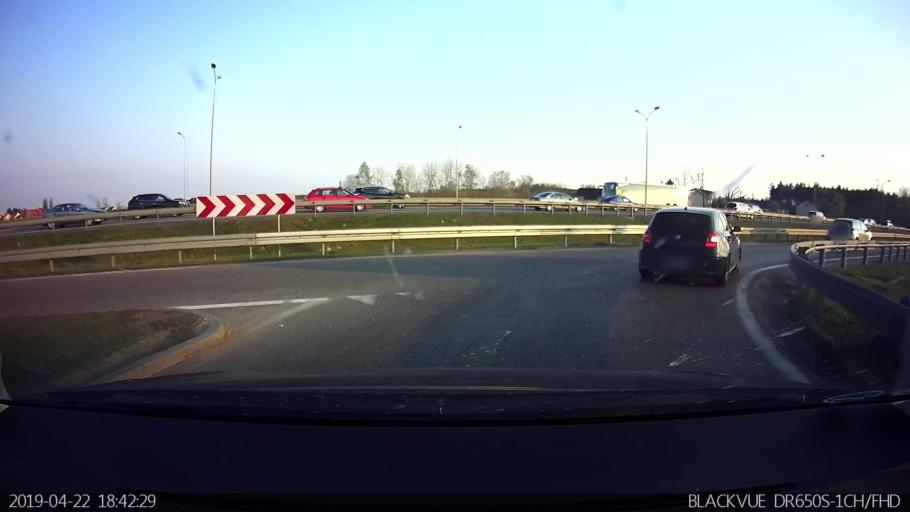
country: PL
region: Masovian Voivodeship
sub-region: Powiat wolominski
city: Dabrowka
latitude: 52.4480
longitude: 21.2620
